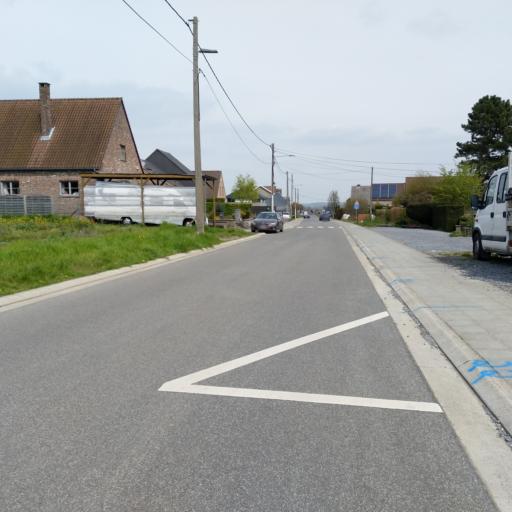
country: BE
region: Wallonia
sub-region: Province du Hainaut
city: Frameries
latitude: 50.3953
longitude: 3.9191
